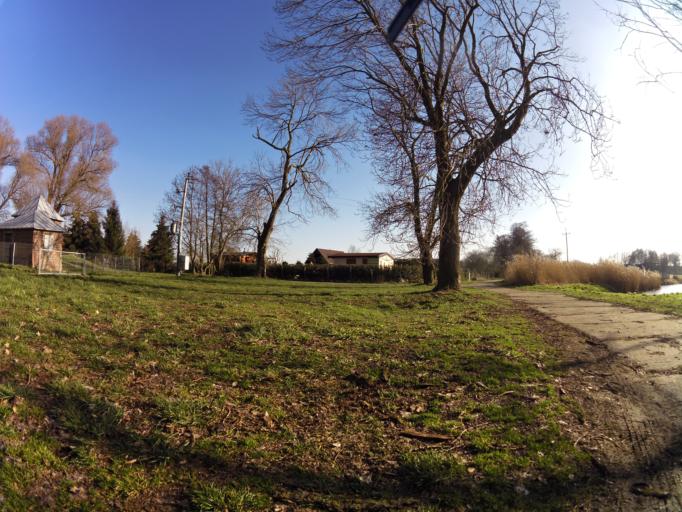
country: PL
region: West Pomeranian Voivodeship
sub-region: Powiat policki
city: Nowe Warpno
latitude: 53.6988
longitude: 14.3667
